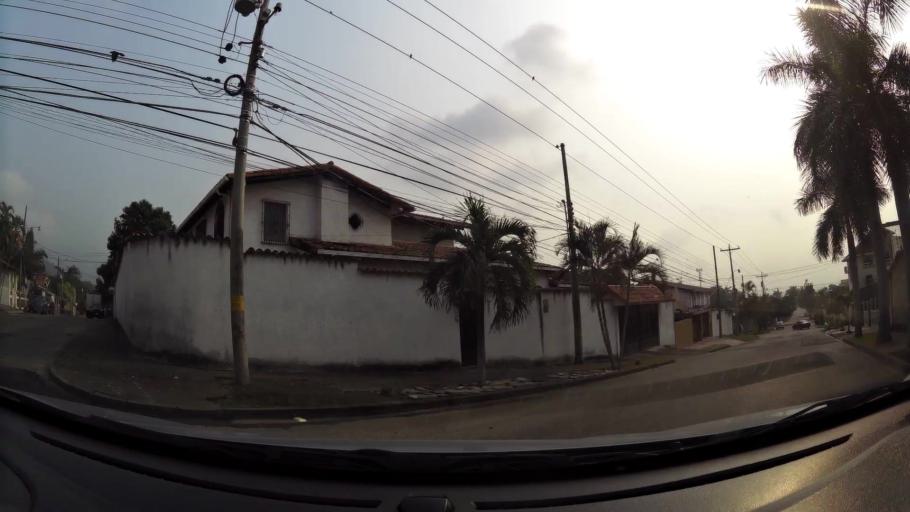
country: HN
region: Cortes
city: Armenta
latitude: 15.4950
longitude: -88.0460
